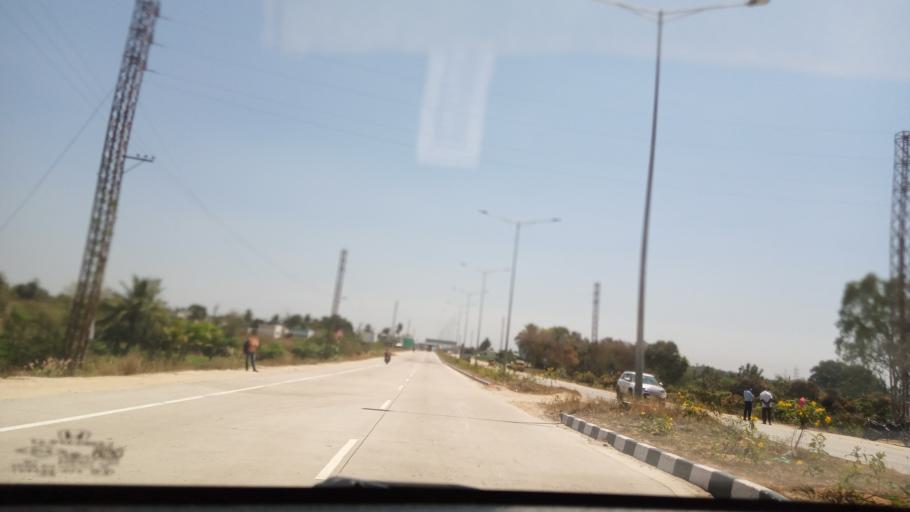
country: IN
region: Andhra Pradesh
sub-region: Chittoor
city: Chittoor
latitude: 13.1954
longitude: 79.0106
